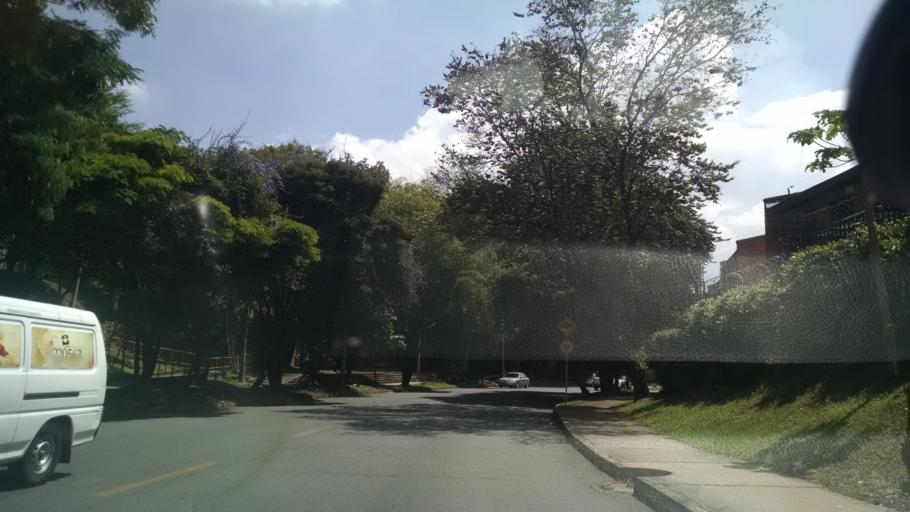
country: CO
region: Antioquia
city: Itagui
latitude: 6.2225
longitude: -75.6017
